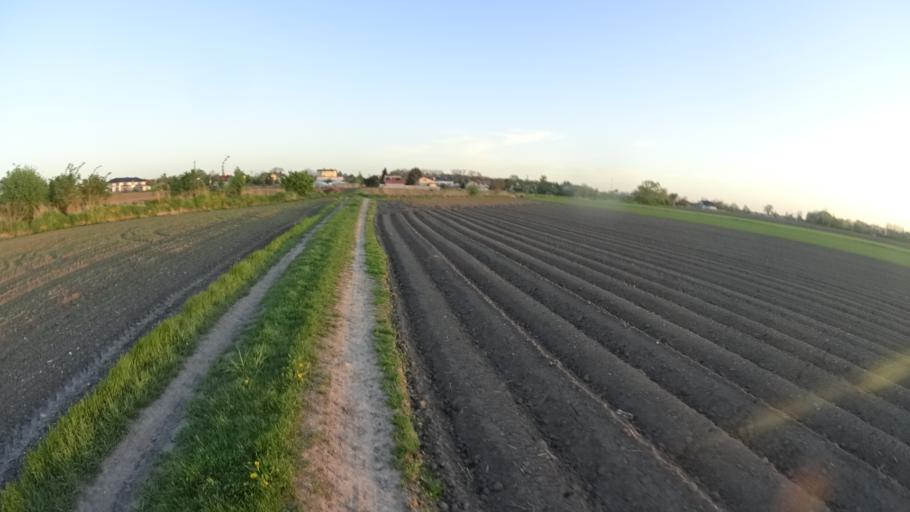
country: PL
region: Masovian Voivodeship
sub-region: Powiat warszawski zachodni
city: Ozarow Mazowiecki
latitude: 52.2253
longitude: 20.7814
